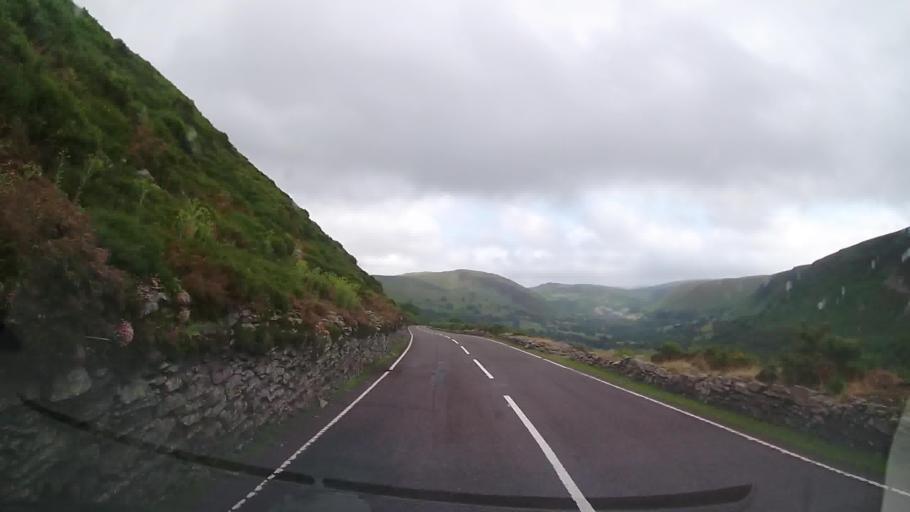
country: GB
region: Wales
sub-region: Sir Powys
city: Llangynog
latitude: 52.8536
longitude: -3.4415
